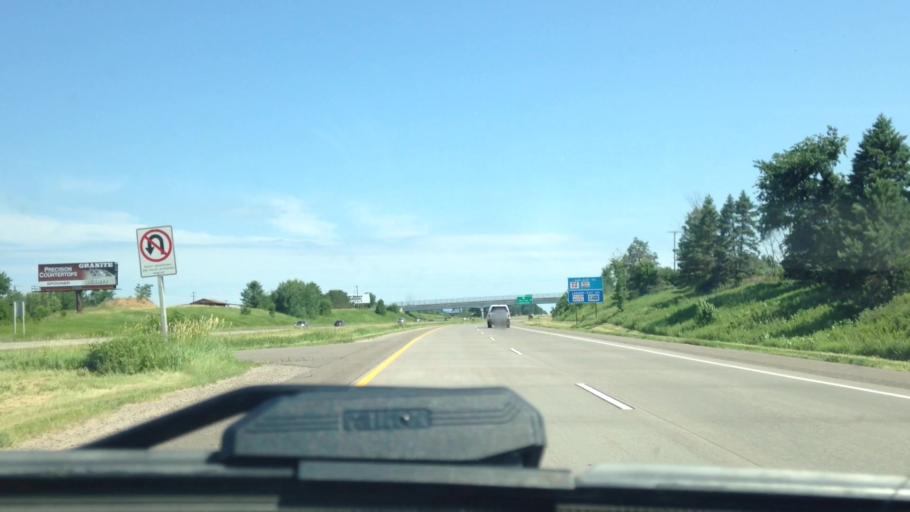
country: US
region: Wisconsin
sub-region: Barron County
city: Rice Lake
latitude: 45.4984
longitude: -91.7638
